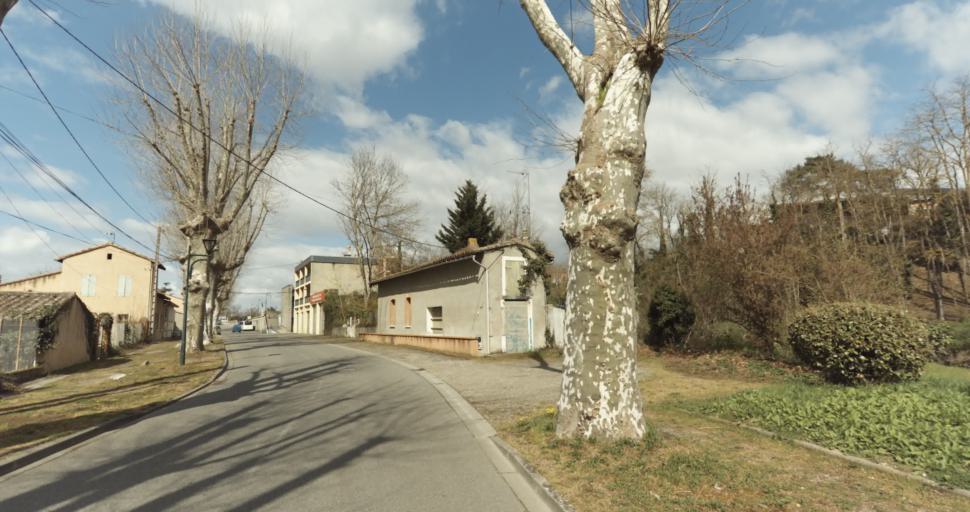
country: FR
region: Midi-Pyrenees
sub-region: Departement de la Haute-Garonne
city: Auterive
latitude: 43.3493
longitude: 1.4780
